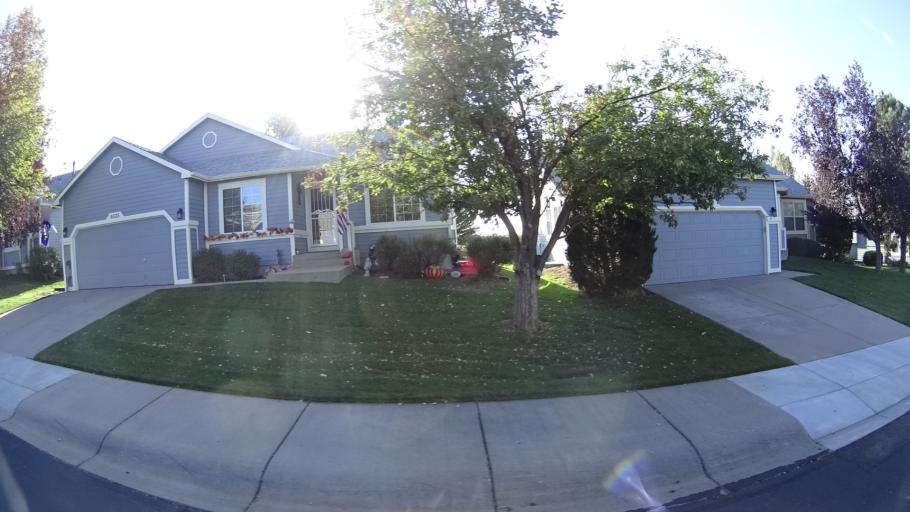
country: US
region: Colorado
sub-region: El Paso County
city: Cimarron Hills
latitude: 38.8896
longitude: -104.7063
